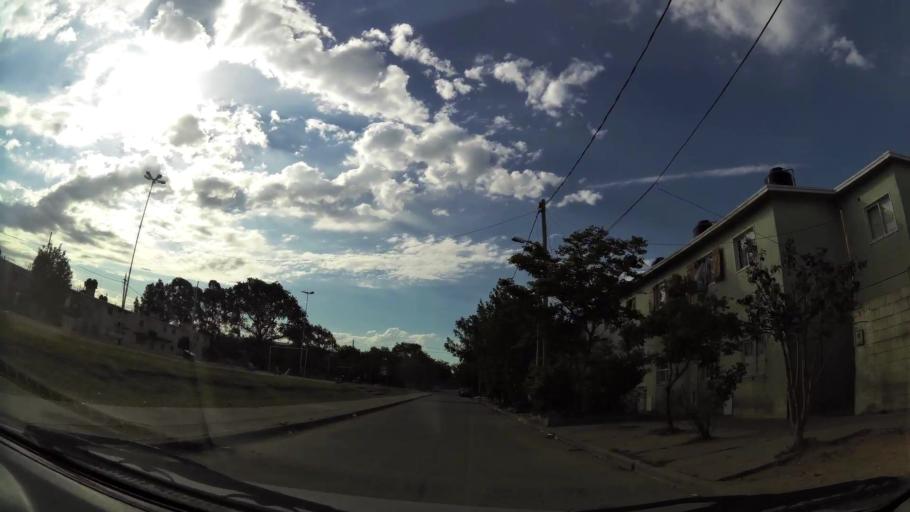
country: AR
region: Buenos Aires
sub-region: Partido de Lanus
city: Lanus
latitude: -34.7005
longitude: -58.3625
